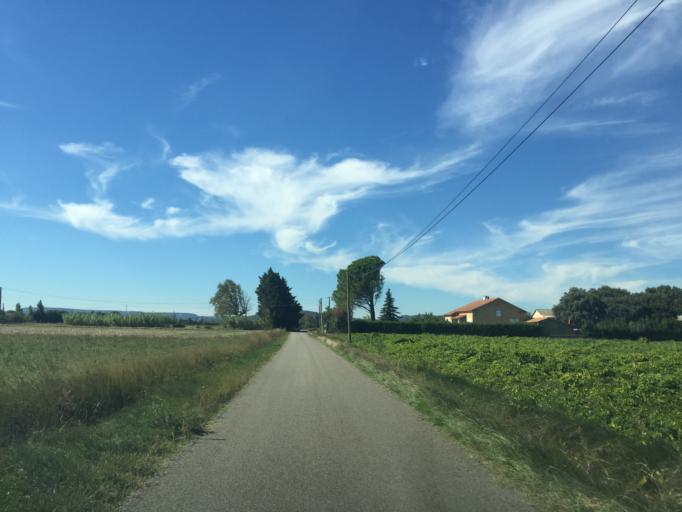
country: FR
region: Provence-Alpes-Cote d'Azur
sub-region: Departement du Vaucluse
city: Orange
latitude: 44.1540
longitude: 4.7846
